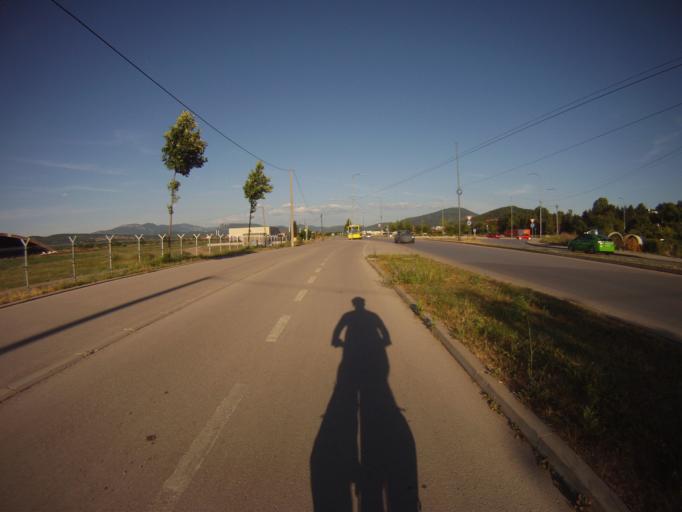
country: RS
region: Central Serbia
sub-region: Nisavski Okrug
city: Nis
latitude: 43.3086
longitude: 21.9463
